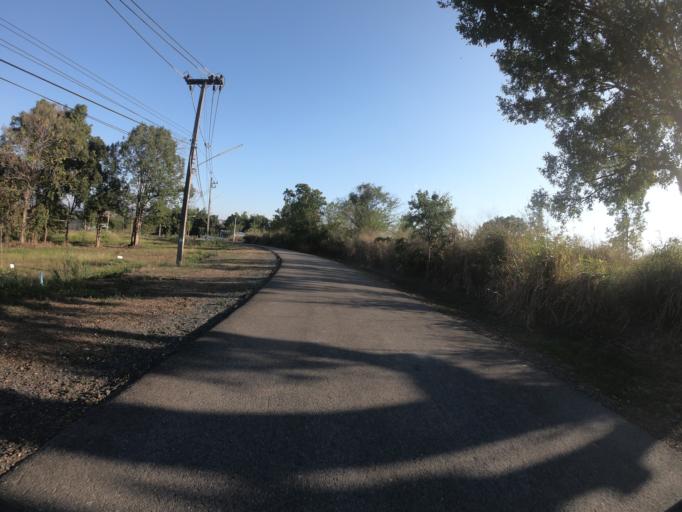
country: TH
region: Chiang Mai
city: Chiang Mai
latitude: 18.7596
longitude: 98.9336
